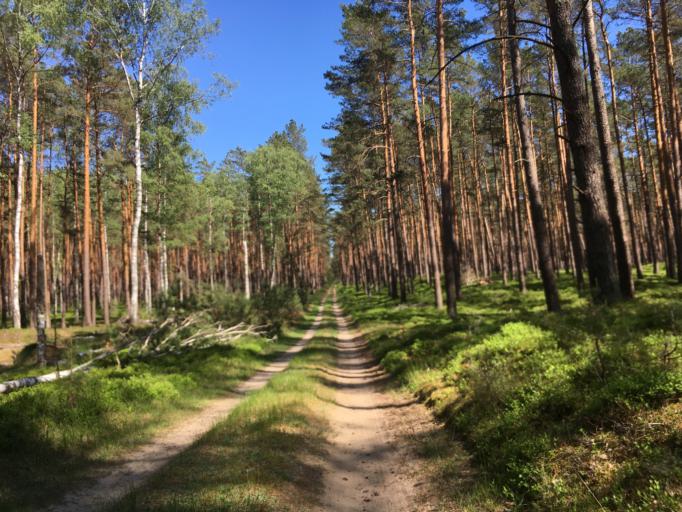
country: DE
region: Brandenburg
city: Friedrichswalde
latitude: 52.9642
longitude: 13.6665
